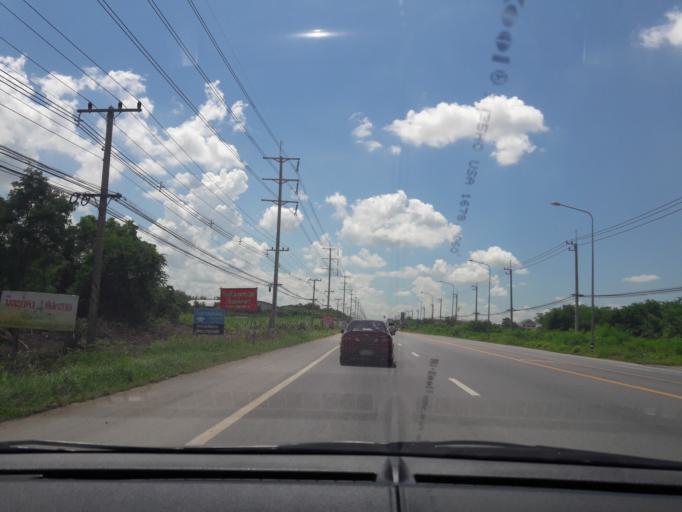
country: TH
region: Nakhon Pathom
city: Kamphaeng Saen
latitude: 14.0149
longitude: 100.0159
